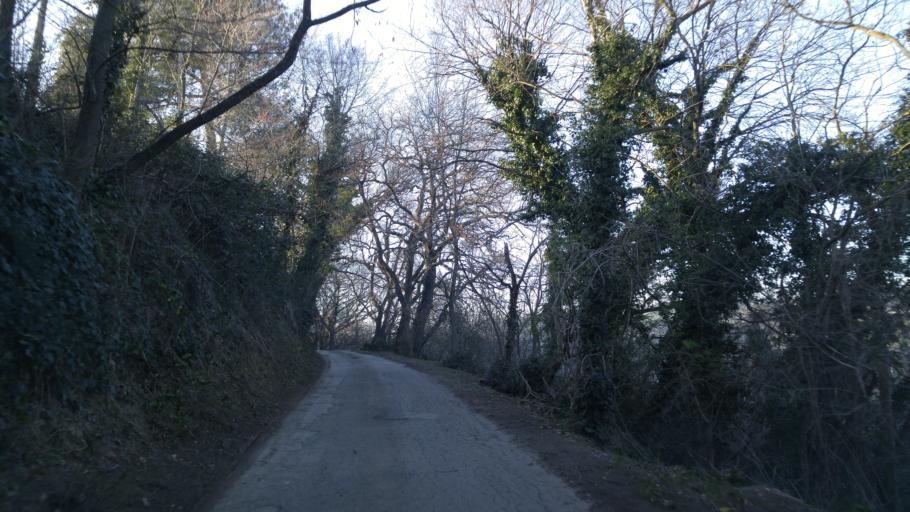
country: IT
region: The Marches
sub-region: Provincia di Pesaro e Urbino
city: Fenile
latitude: 43.8534
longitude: 12.9497
